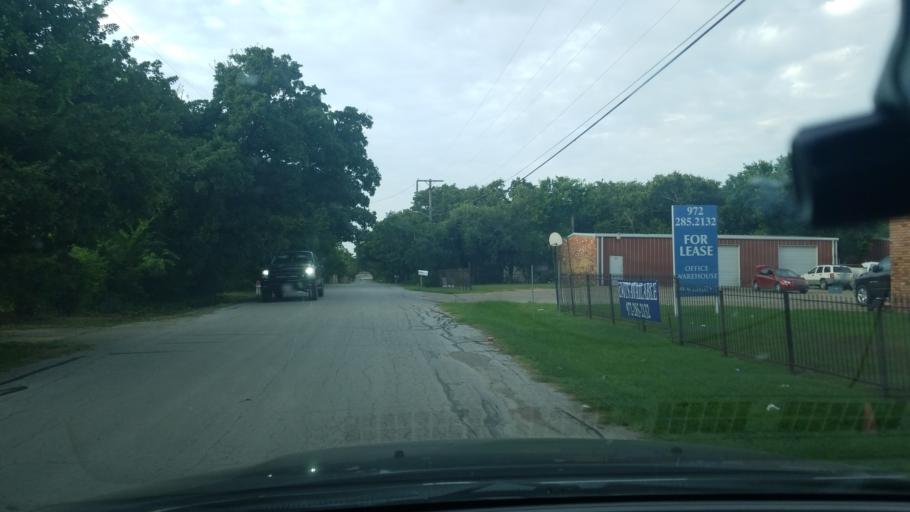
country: US
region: Texas
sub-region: Dallas County
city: Balch Springs
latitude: 32.7383
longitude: -96.6341
